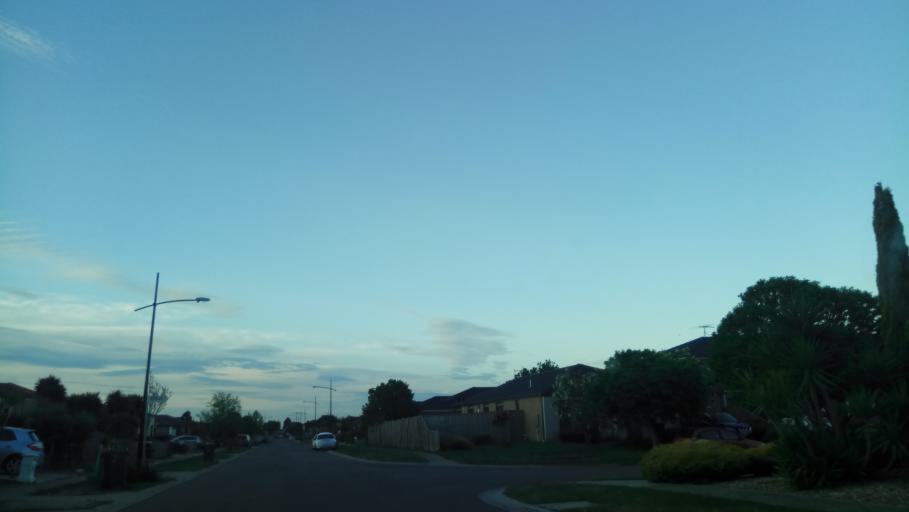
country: AU
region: Victoria
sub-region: Wyndham
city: Point Cook
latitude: -37.9046
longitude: 144.7451
